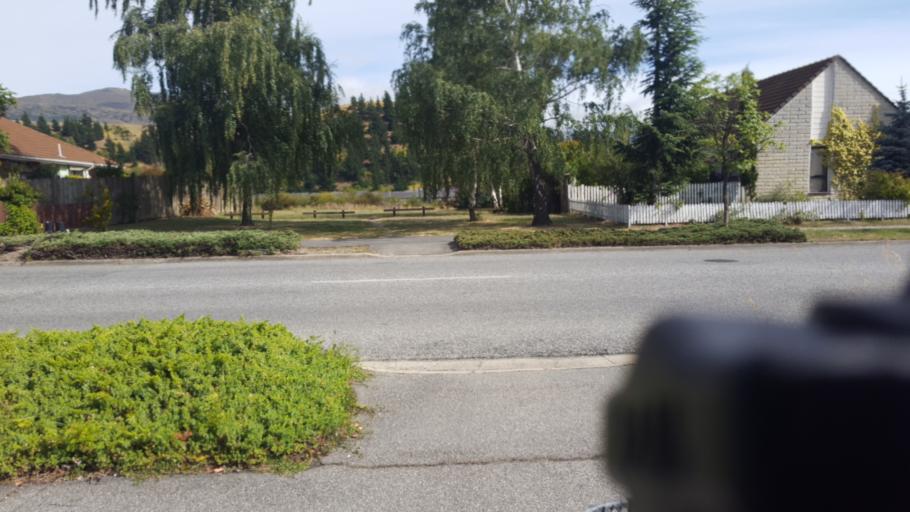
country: NZ
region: Otago
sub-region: Queenstown-Lakes District
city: Wanaka
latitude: -45.0391
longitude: 169.1905
